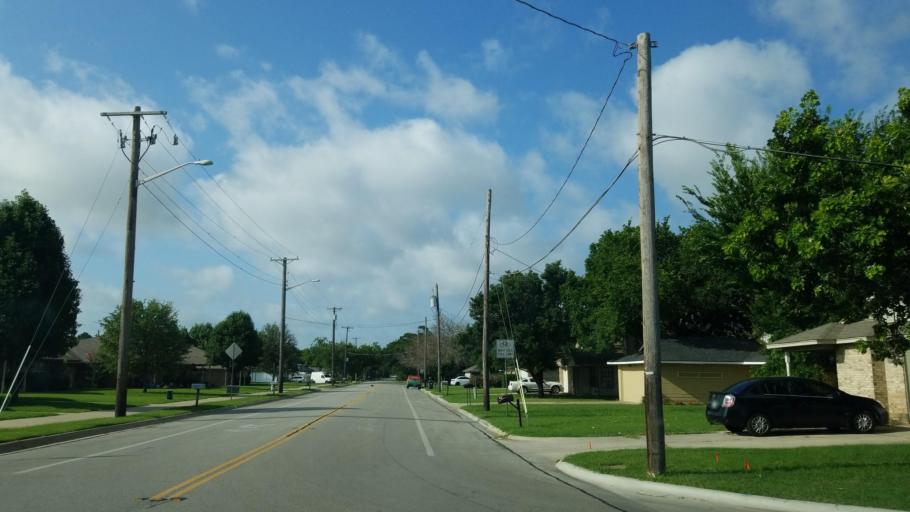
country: US
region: Texas
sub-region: Denton County
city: Denton
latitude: 33.2208
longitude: -97.0964
